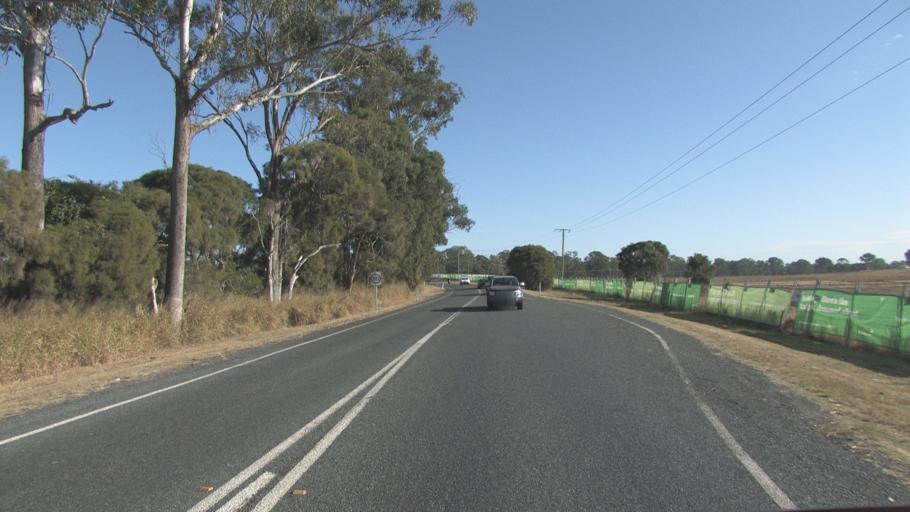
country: AU
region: Queensland
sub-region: Logan
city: North Maclean
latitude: -27.8235
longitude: 153.0090
